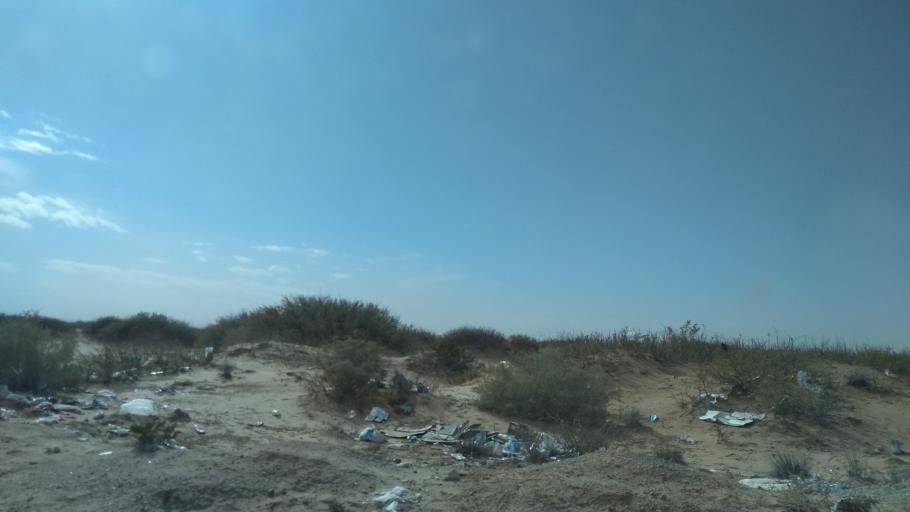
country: US
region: Texas
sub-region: El Paso County
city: San Elizario
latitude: 31.5762
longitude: -106.3323
